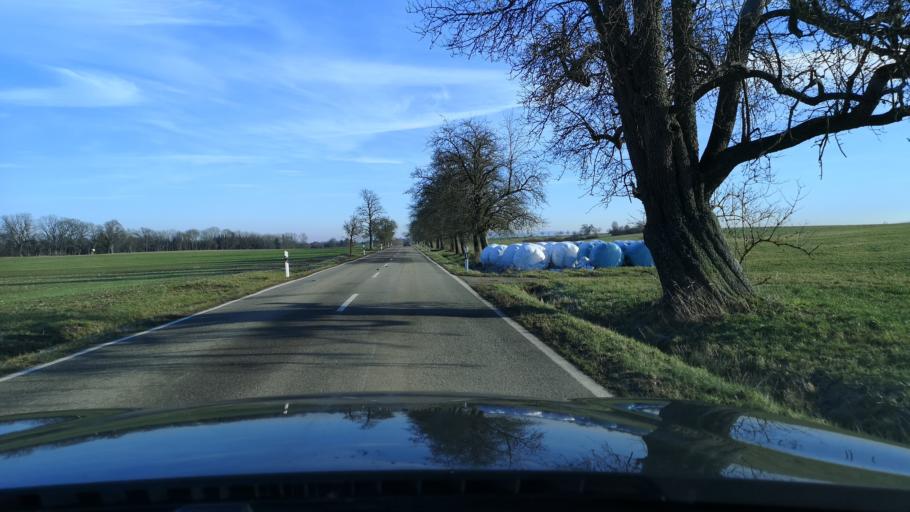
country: DE
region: Baden-Wuerttemberg
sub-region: Regierungsbezirk Stuttgart
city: Obergroningen
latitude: 48.8928
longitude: 9.9158
